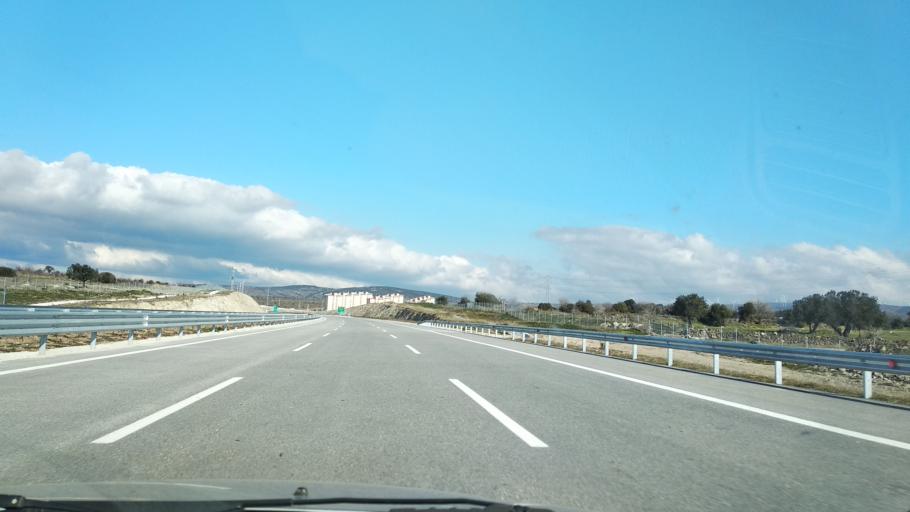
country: TR
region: Izmir
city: Yenisakran
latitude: 38.8698
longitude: 27.0841
